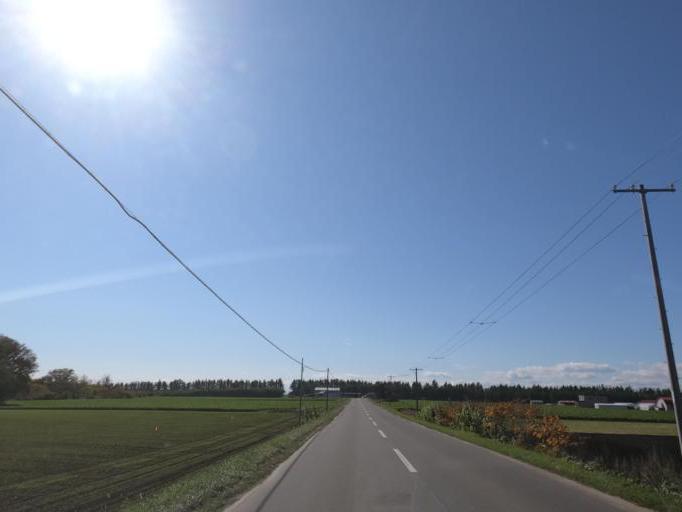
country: JP
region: Hokkaido
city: Obihiro
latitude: 42.8183
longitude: 143.2559
